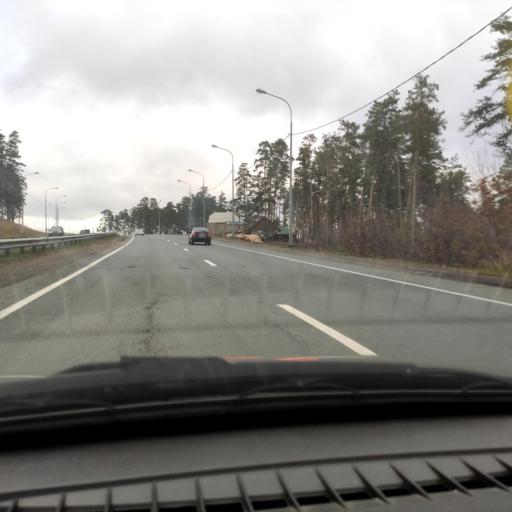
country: RU
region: Samara
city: Zhigulevsk
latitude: 53.5363
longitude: 49.5166
